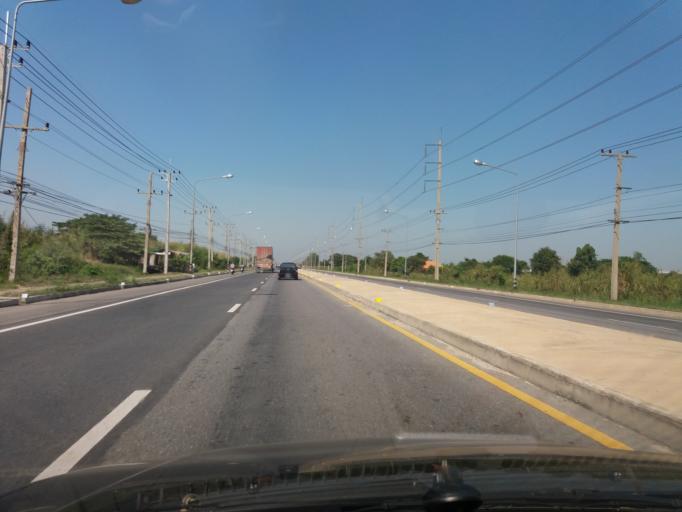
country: TH
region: Chai Nat
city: Manorom
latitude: 15.2868
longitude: 100.0972
